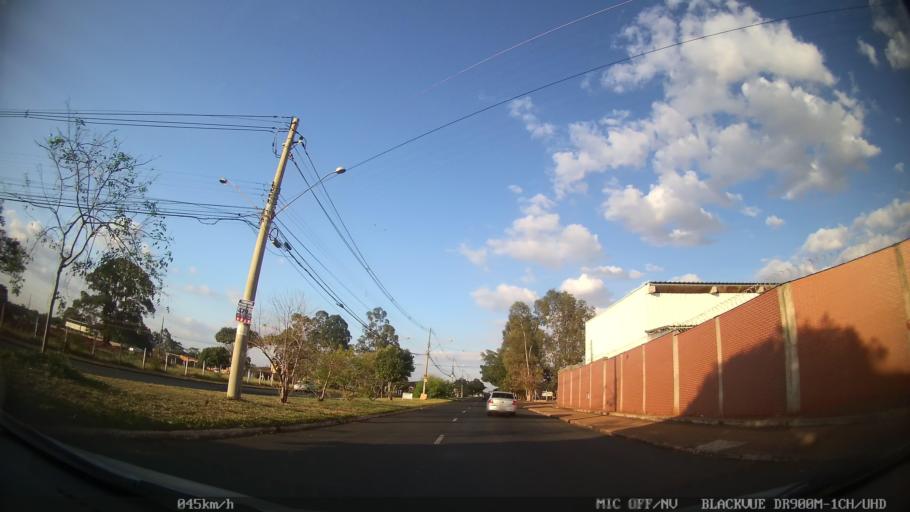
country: BR
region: Sao Paulo
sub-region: Ribeirao Preto
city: Ribeirao Preto
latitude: -21.1628
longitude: -47.7411
